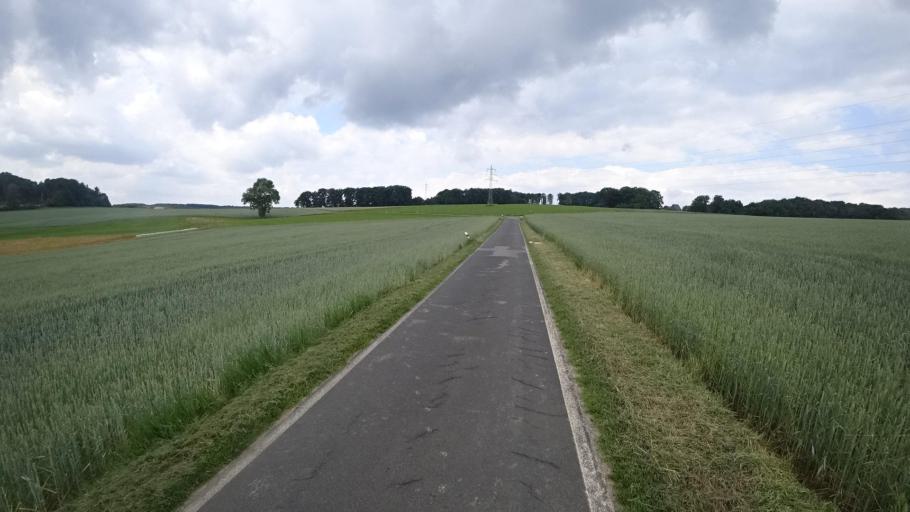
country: DE
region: Rheinland-Pfalz
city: Bachenberg
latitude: 50.7078
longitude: 7.6470
